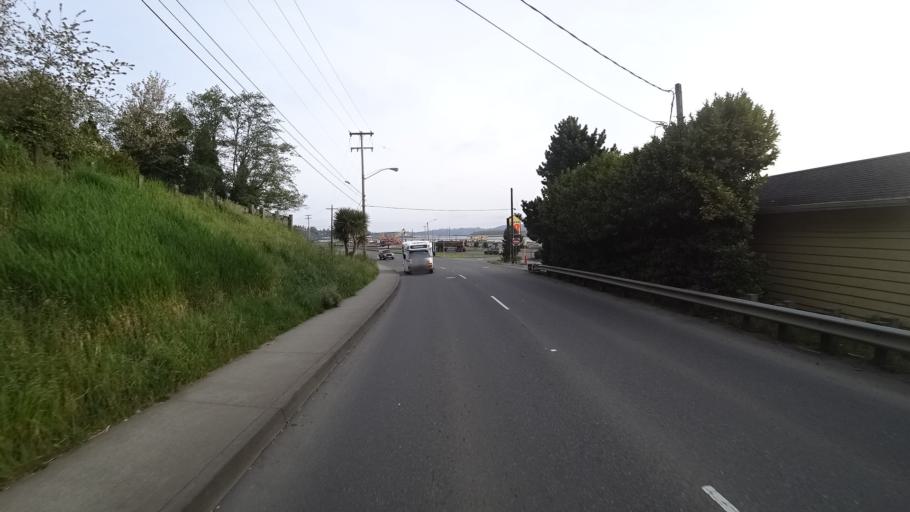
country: US
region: Oregon
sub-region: Coos County
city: Coos Bay
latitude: 43.3746
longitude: -124.2131
